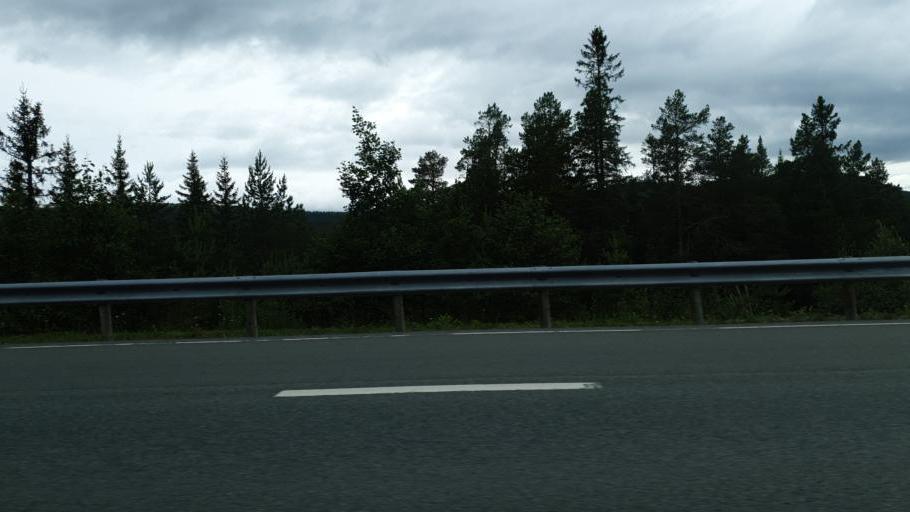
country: NO
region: Sor-Trondelag
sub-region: Rennebu
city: Berkak
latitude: 62.7910
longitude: 10.0040
